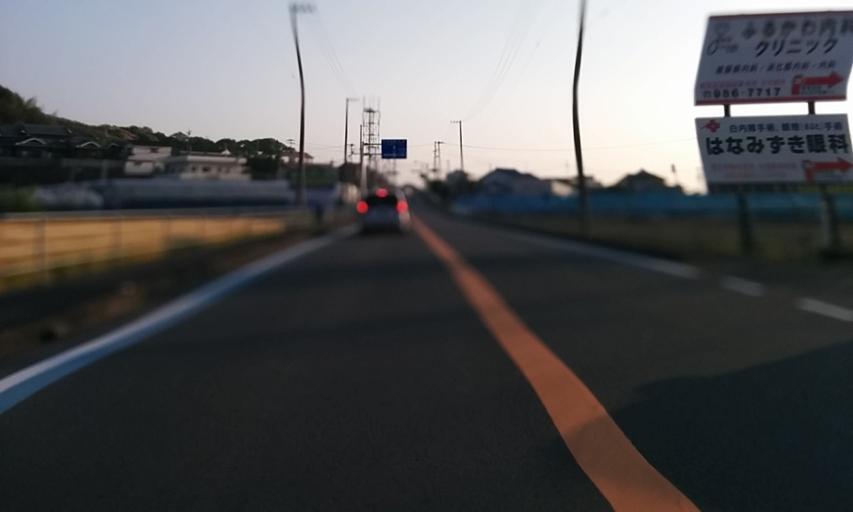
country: JP
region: Ehime
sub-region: Shikoku-chuo Shi
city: Matsuyama
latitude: 33.7863
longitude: 132.7656
